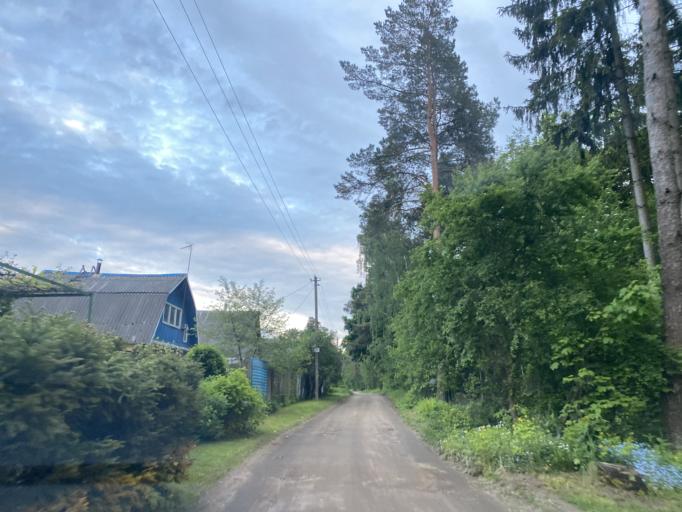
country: BY
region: Minsk
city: Rudzyensk
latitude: 53.6086
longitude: 27.7853
